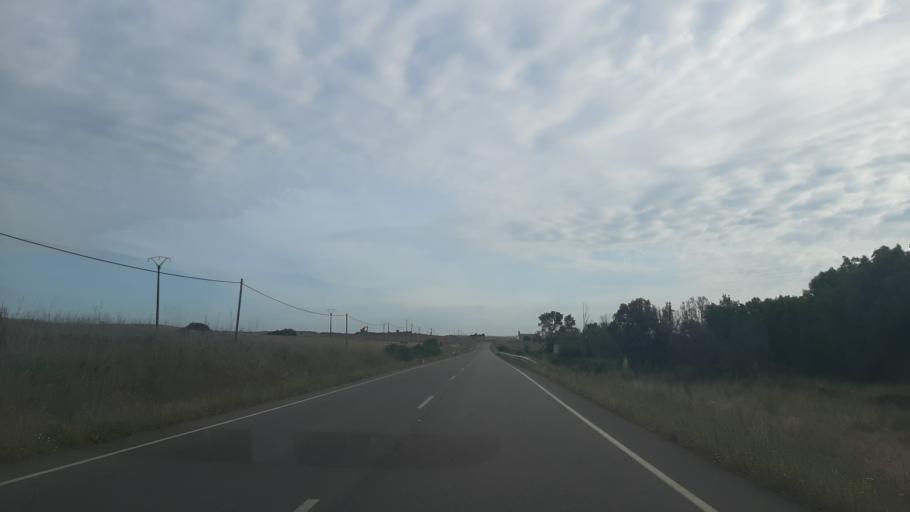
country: ES
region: Castille and Leon
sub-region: Provincia de Salamanca
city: Gallegos de Arganan
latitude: 40.6159
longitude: -6.7060
